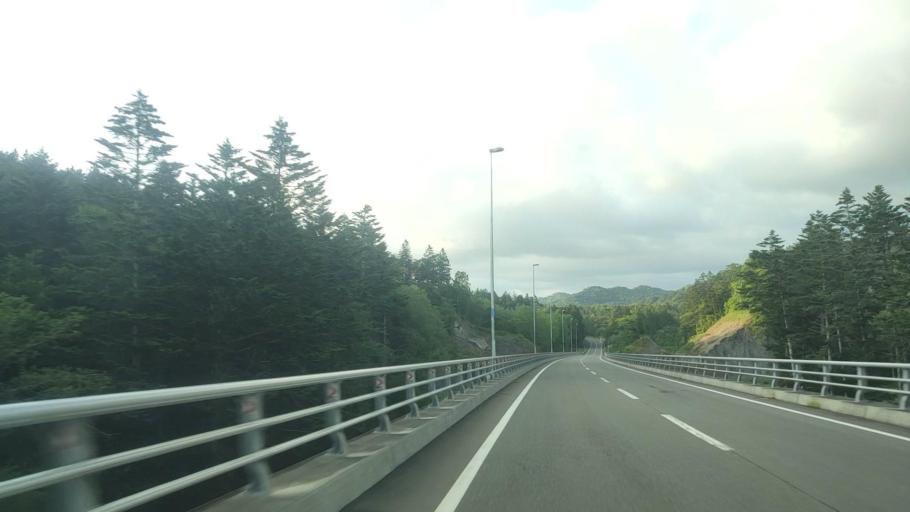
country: JP
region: Hokkaido
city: Bibai
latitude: 43.1083
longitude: 142.0983
